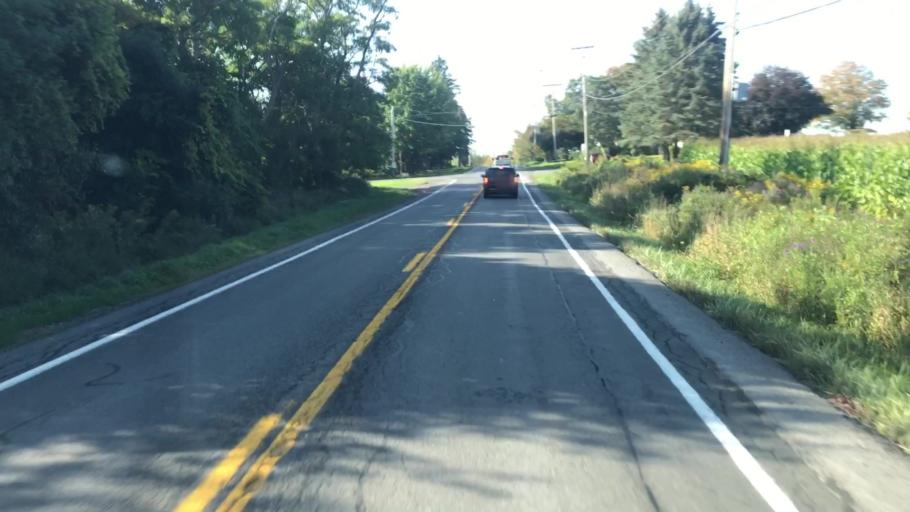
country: US
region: New York
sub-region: Onondaga County
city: Elbridge
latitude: 42.9938
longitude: -76.4277
